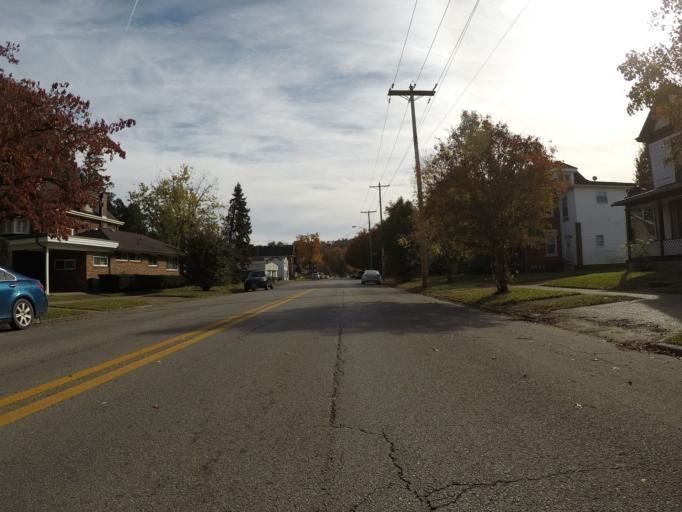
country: US
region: West Virginia
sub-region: Cabell County
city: Huntington
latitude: 38.4132
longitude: -82.4400
